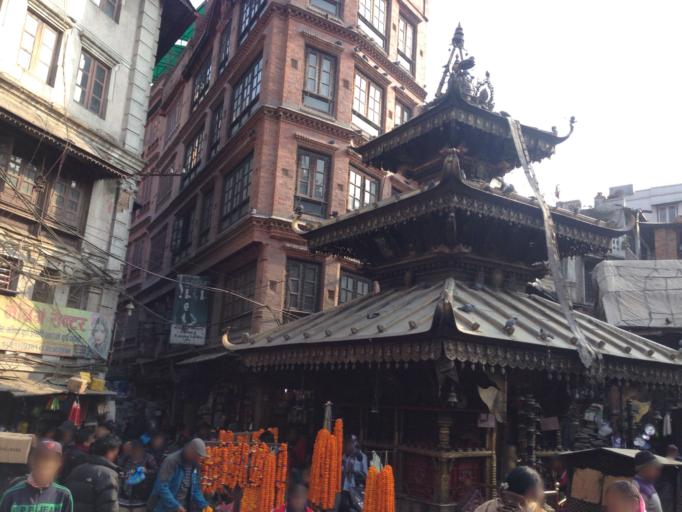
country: NP
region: Central Region
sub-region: Bagmati Zone
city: Kathmandu
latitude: 27.7075
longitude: 85.3120
